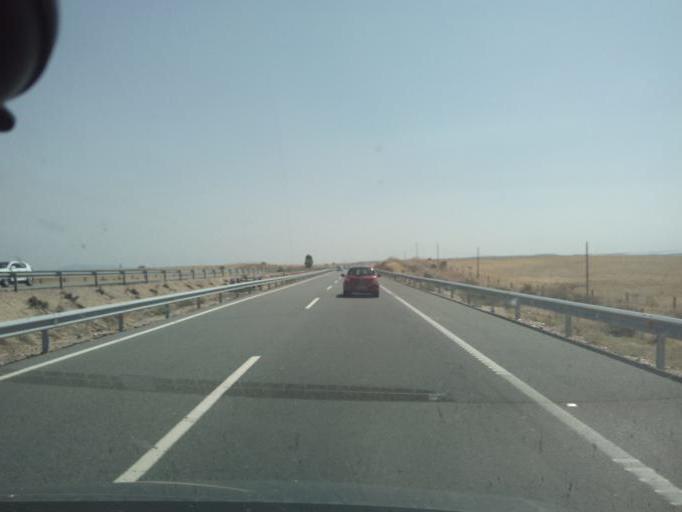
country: ES
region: Extremadura
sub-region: Provincia de Caceres
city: Peraleda de la Mata
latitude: 39.8919
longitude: -5.3956
